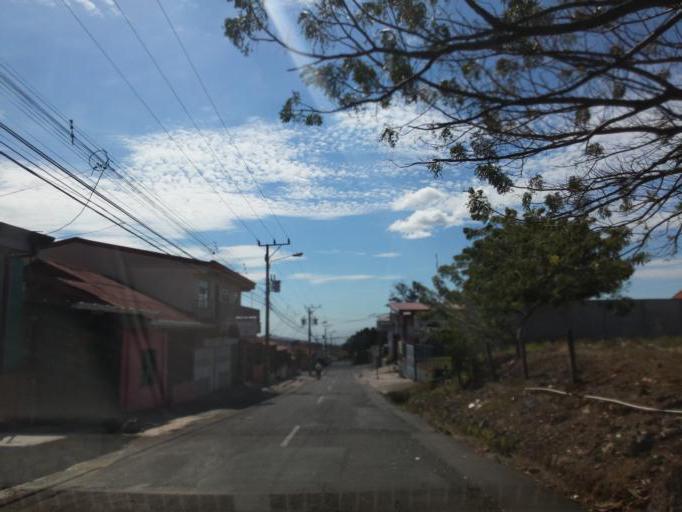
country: CR
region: Heredia
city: Santo Domingo
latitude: 10.0380
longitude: -84.1602
